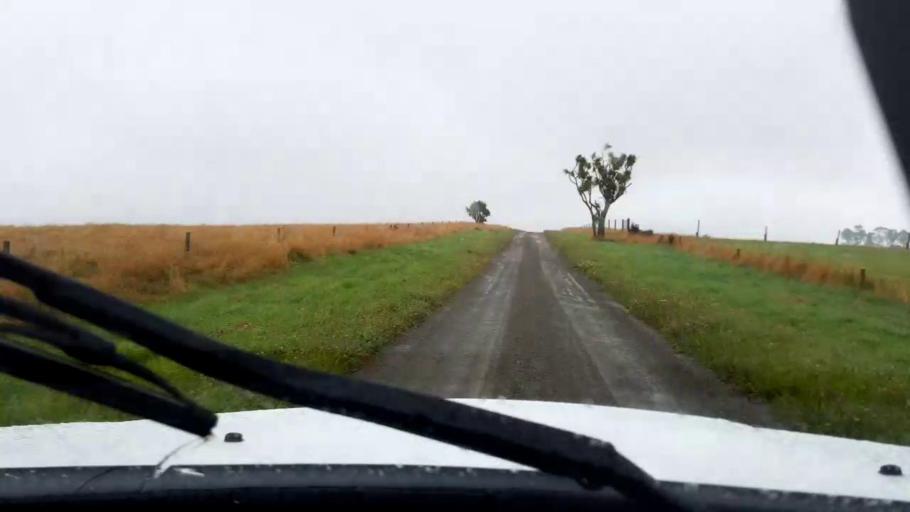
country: NZ
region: Canterbury
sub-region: Timaru District
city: Pleasant Point
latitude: -44.1690
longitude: 171.1633
